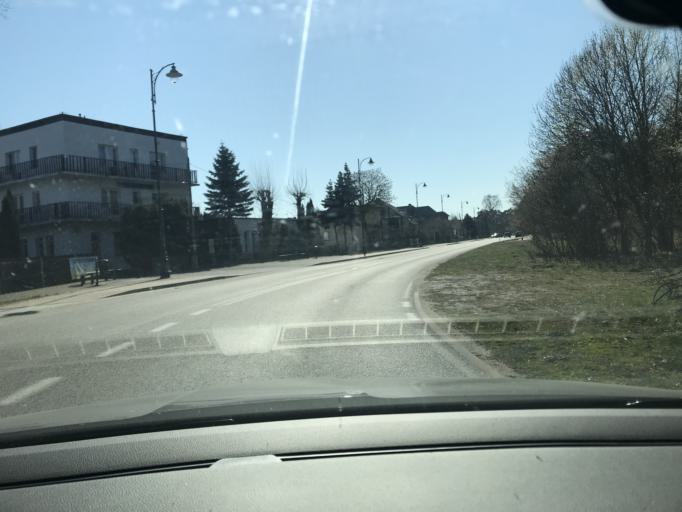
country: PL
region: Pomeranian Voivodeship
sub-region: Powiat nowodworski
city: Krynica Morska
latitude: 54.3727
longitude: 19.4197
